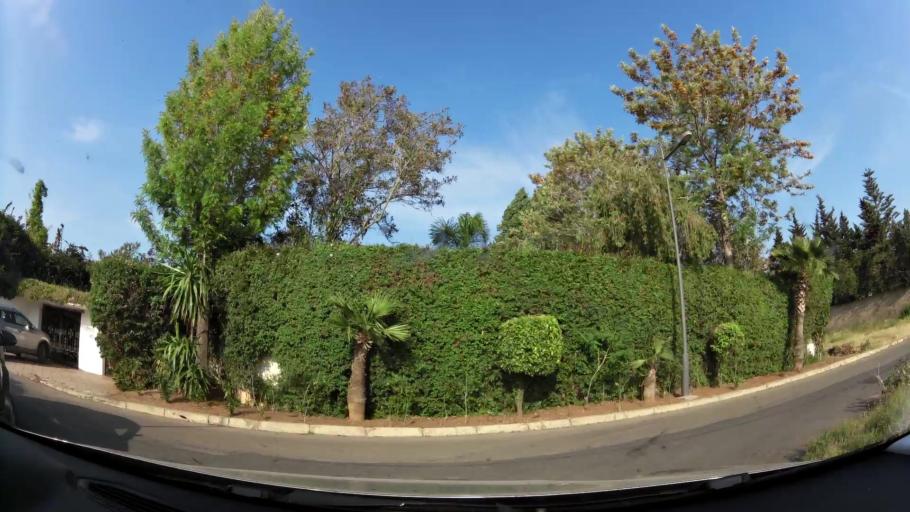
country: MA
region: Rabat-Sale-Zemmour-Zaer
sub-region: Rabat
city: Rabat
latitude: 33.9403
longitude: -6.8172
